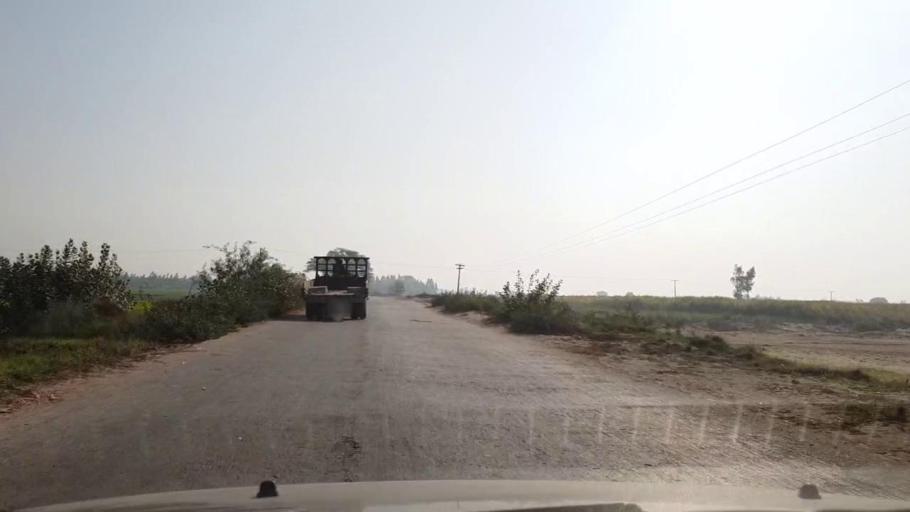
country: PK
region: Sindh
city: Matiari
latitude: 25.5655
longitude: 68.5184
